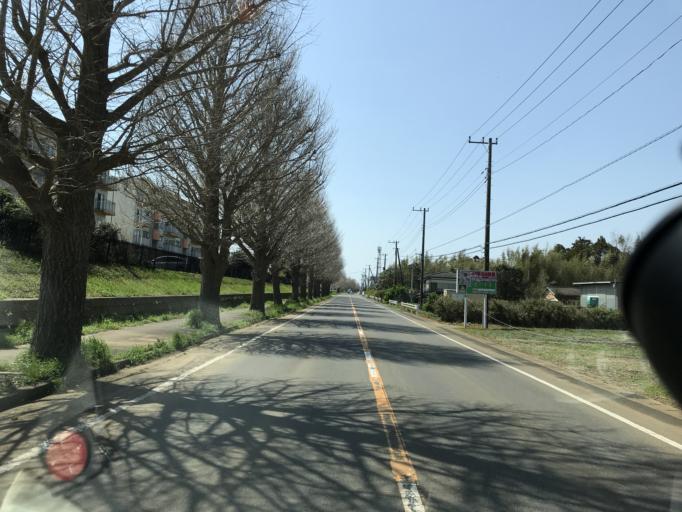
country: JP
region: Chiba
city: Asahi
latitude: 35.7902
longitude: 140.7071
